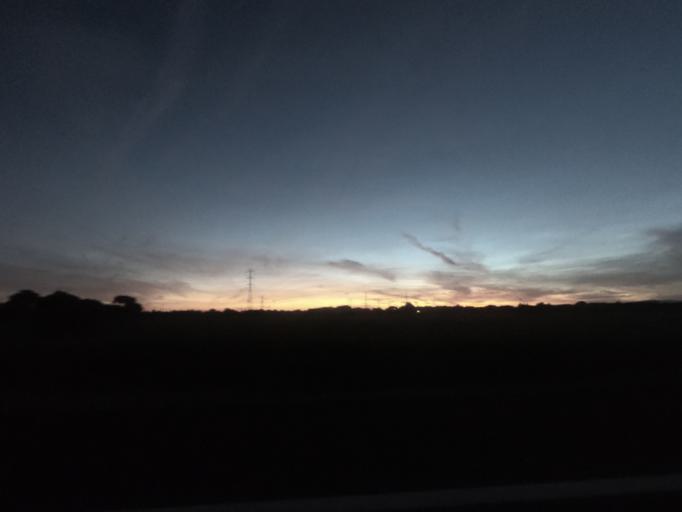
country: PT
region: Santarem
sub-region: Benavente
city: Benavente
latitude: 38.9178
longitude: -8.8040
